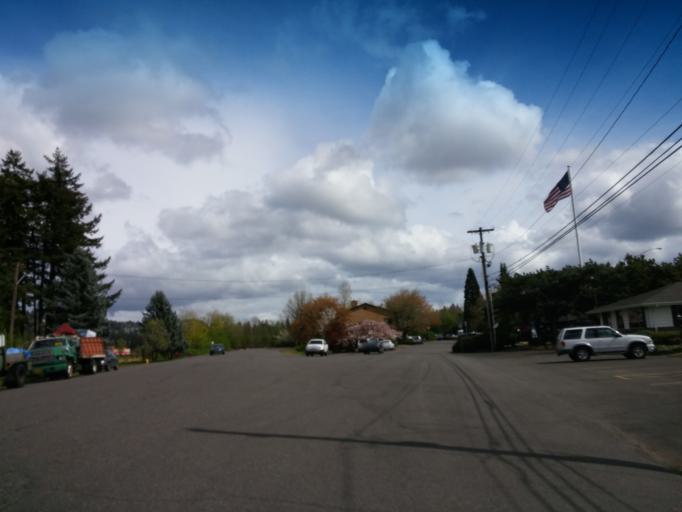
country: US
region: Oregon
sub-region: Washington County
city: Cedar Hills
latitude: 45.5160
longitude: -122.7970
